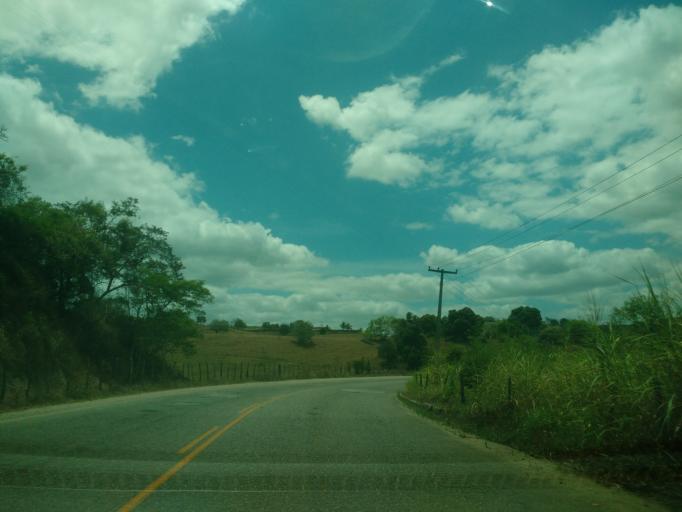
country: BR
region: Alagoas
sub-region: Santana Do Mundau
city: Santana do Mundau
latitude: -9.1454
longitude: -36.1655
